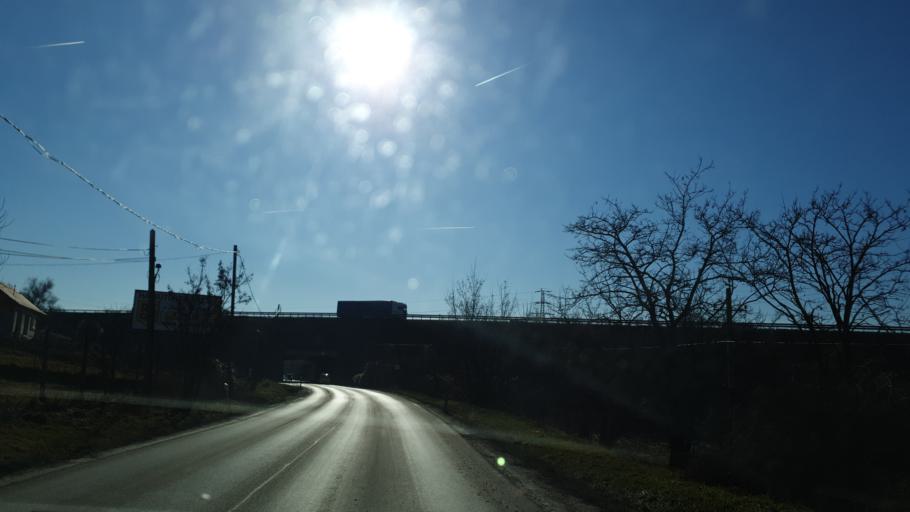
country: HU
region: Pest
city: Paty
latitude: 47.4940
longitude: 18.8246
